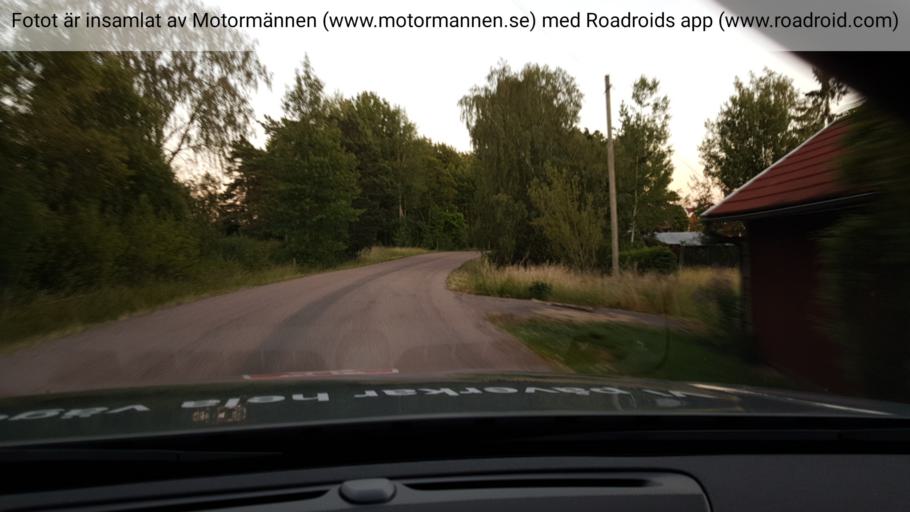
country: SE
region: Vaestmanland
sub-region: Hallstahammars Kommun
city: Kolback
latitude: 59.5339
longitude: 16.1524
